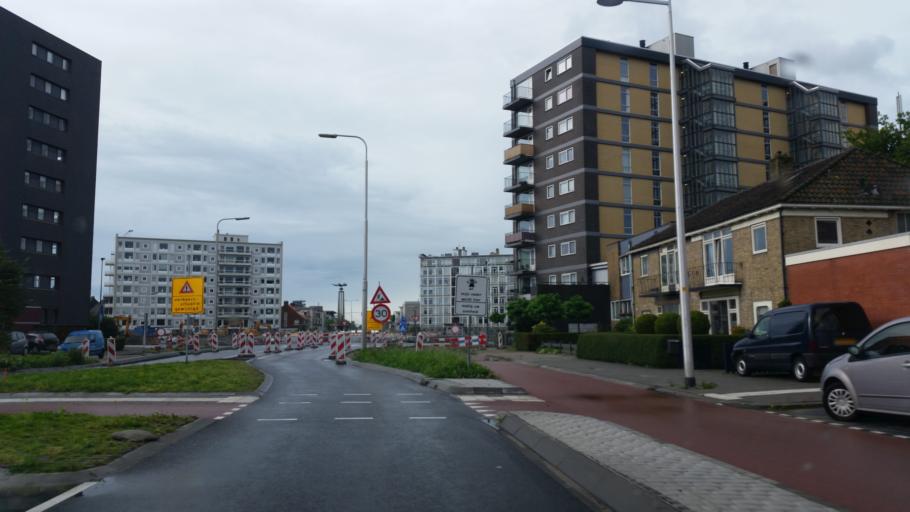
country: NL
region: Friesland
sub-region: Gemeente Leeuwarden
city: Bilgaard
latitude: 53.2063
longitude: 5.7766
